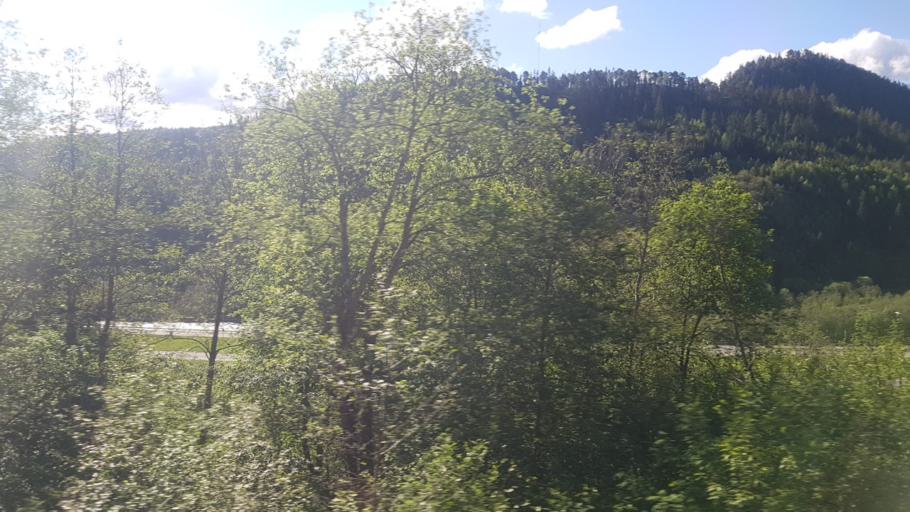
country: NO
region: Sor-Trondelag
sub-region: Midtre Gauldal
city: Storen
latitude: 63.0226
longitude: 10.2562
